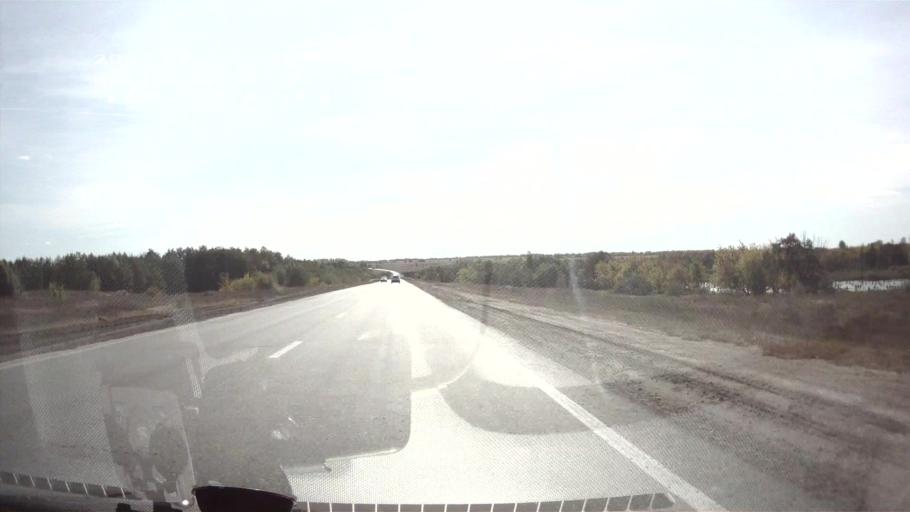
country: RU
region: Samara
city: Varlamovo
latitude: 53.1412
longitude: 48.2852
